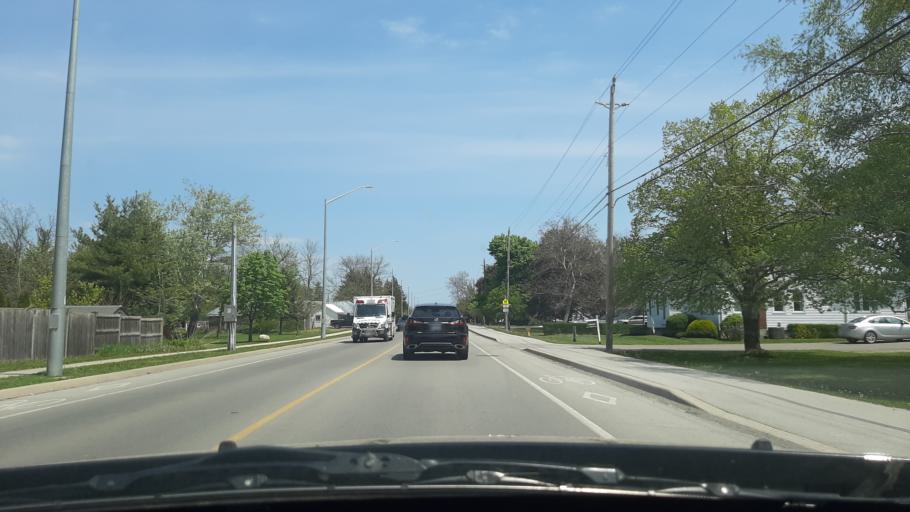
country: US
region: New York
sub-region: Niagara County
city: Youngstown
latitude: 43.2139
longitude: -79.1325
